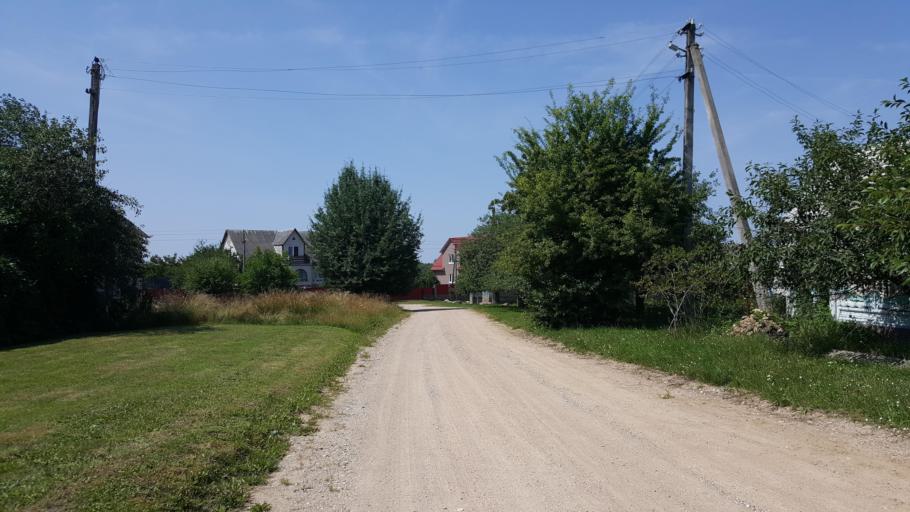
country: BY
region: Brest
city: Vysokaye
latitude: 52.3598
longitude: 23.3858
